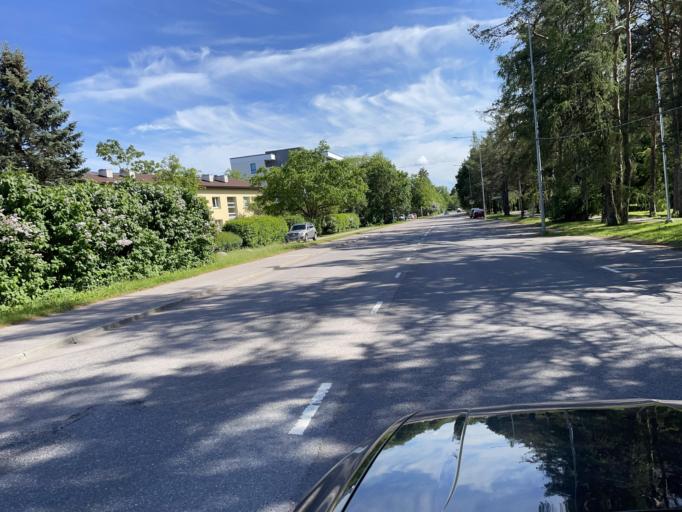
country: EE
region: Harju
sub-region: Keila linn
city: Keila
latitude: 59.3135
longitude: 24.4139
